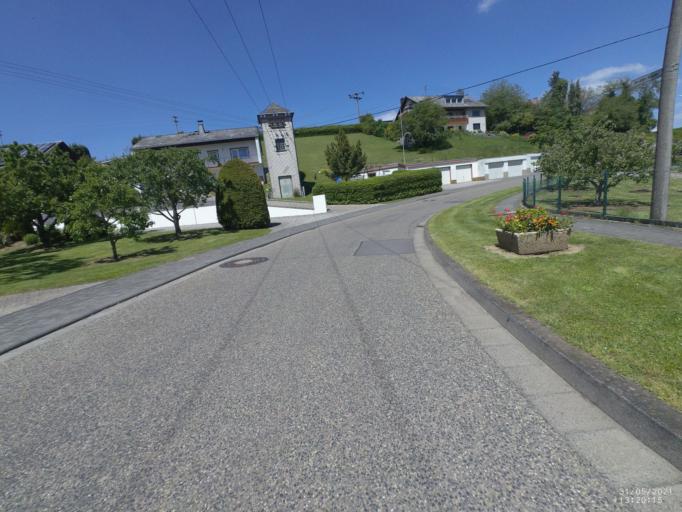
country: DE
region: Rheinland-Pfalz
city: Winningen
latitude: 50.2872
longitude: 7.5165
